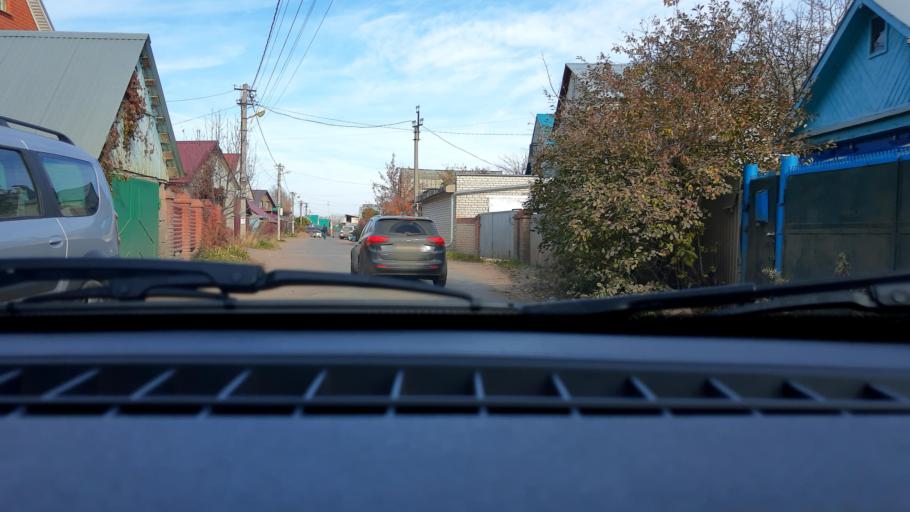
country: RU
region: Bashkortostan
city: Mikhaylovka
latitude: 54.7803
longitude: 55.8949
